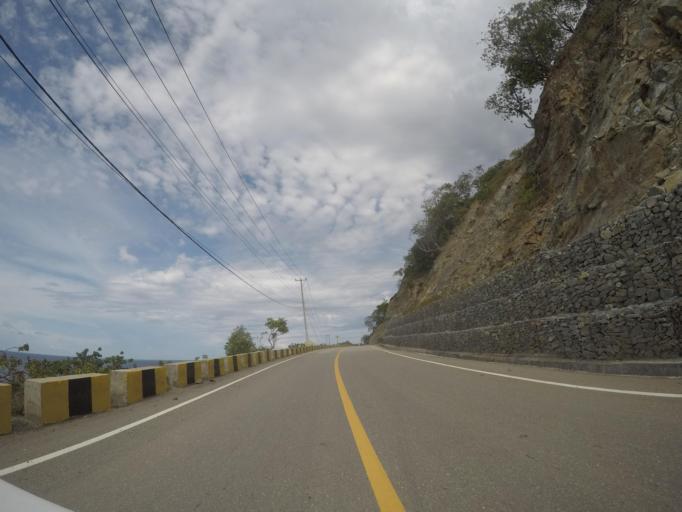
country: TL
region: Liquica
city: Maubara
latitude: -8.6239
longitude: 125.1665
